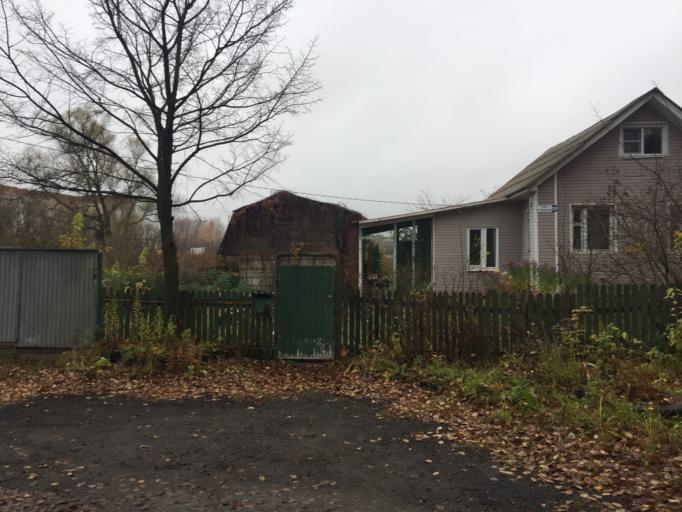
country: RU
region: Jaroslavl
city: Yaroslavl
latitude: 57.7155
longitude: 39.7698
